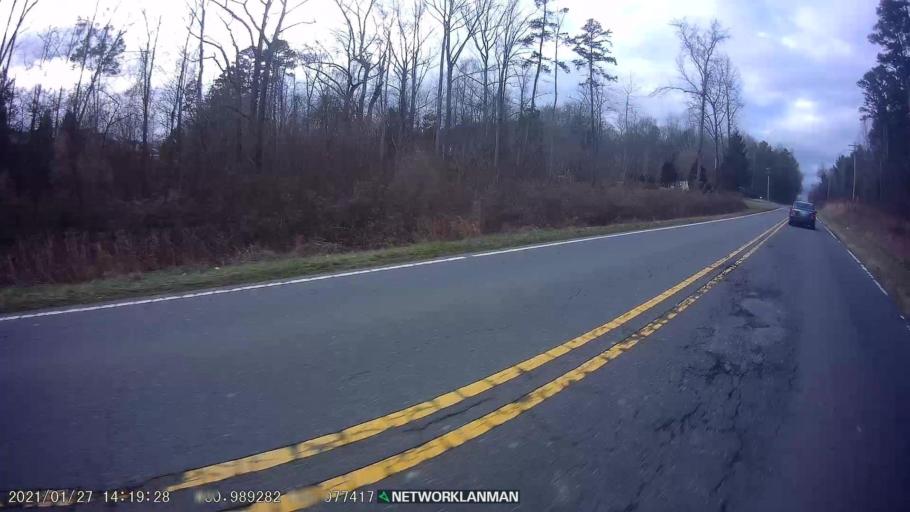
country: US
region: South Carolina
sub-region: York County
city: Lake Wylie
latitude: 35.0775
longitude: -80.9894
